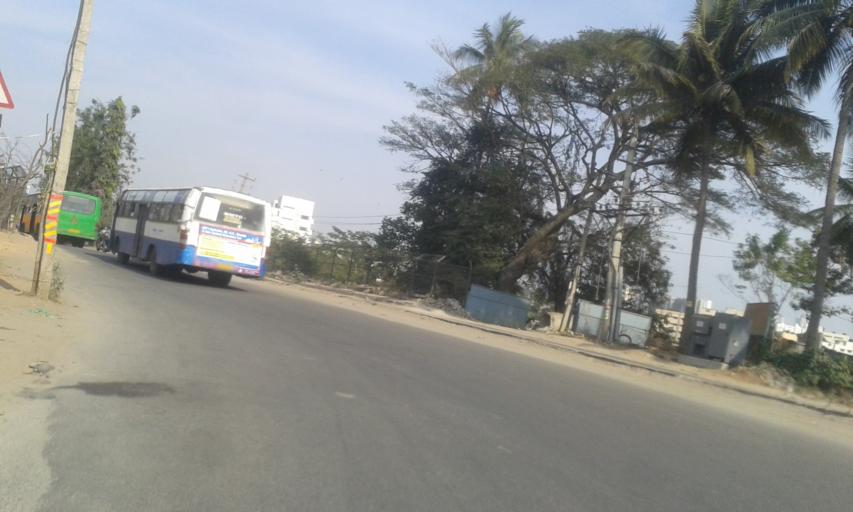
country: IN
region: Karnataka
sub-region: Bangalore Urban
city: Bangalore
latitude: 12.9357
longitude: 77.5133
